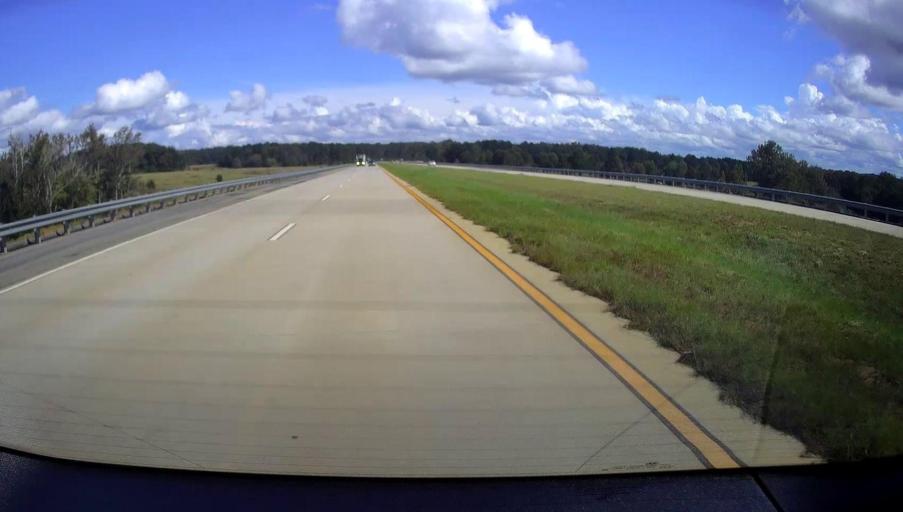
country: US
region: Georgia
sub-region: Jones County
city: Gray
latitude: 33.0289
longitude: -83.5332
